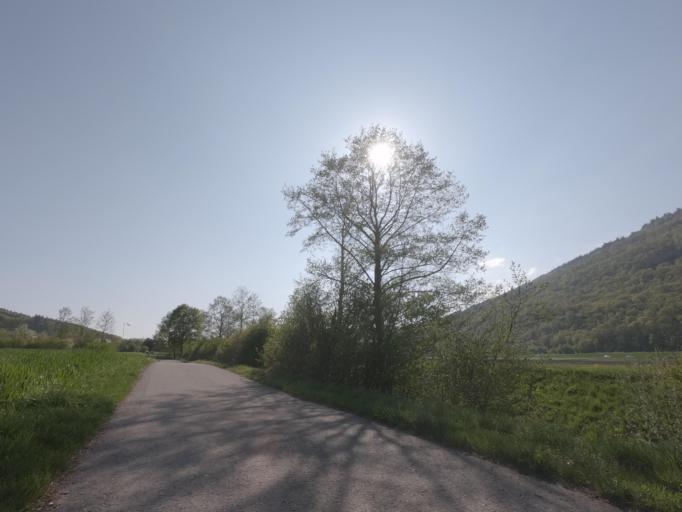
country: CH
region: Bern
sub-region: Biel/Bienne District
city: Orpund
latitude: 47.1650
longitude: 7.3005
